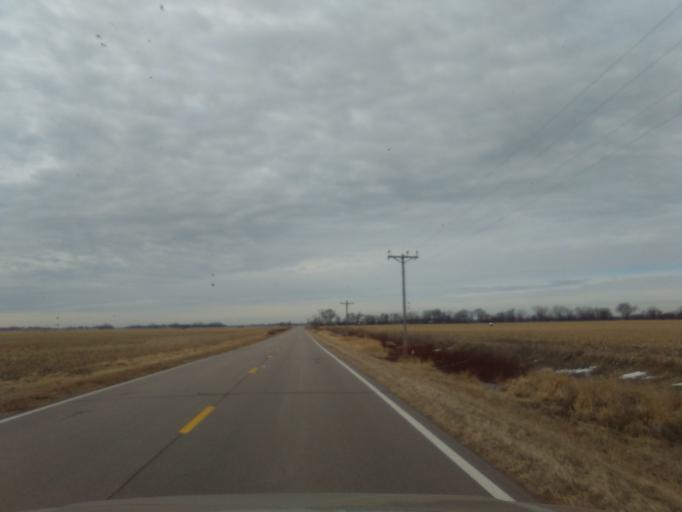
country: US
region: Nebraska
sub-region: Hall County
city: Grand Island
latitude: 40.7710
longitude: -98.4262
